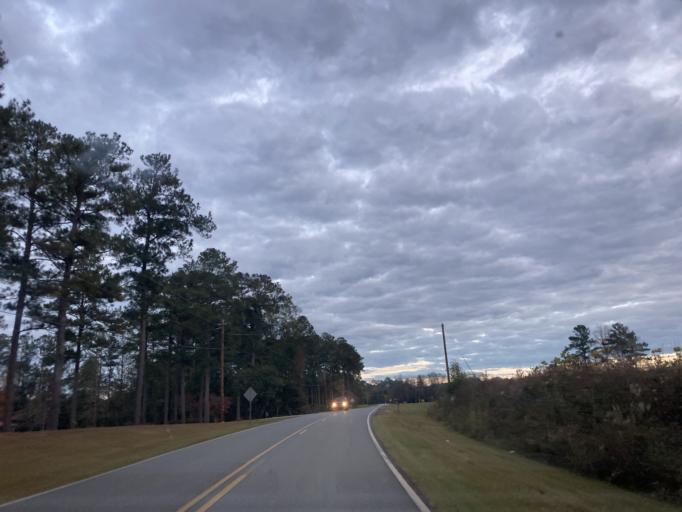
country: US
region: Georgia
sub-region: Jones County
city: Gray
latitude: 32.9744
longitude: -83.5226
